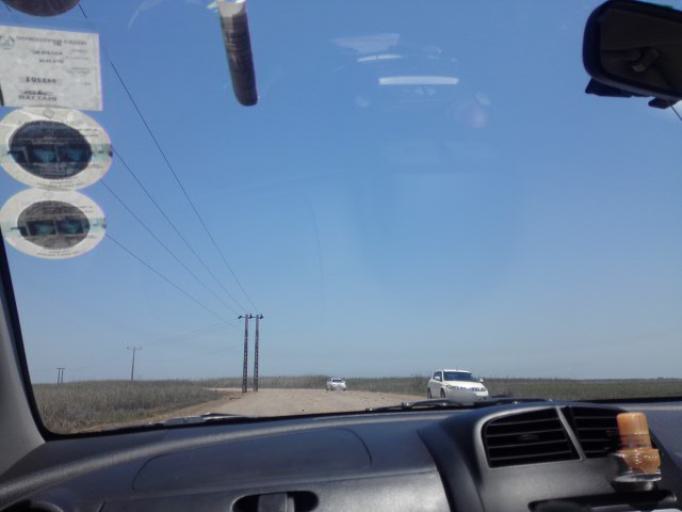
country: MZ
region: Maputo City
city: Maputo
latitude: -25.7328
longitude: 32.7210
